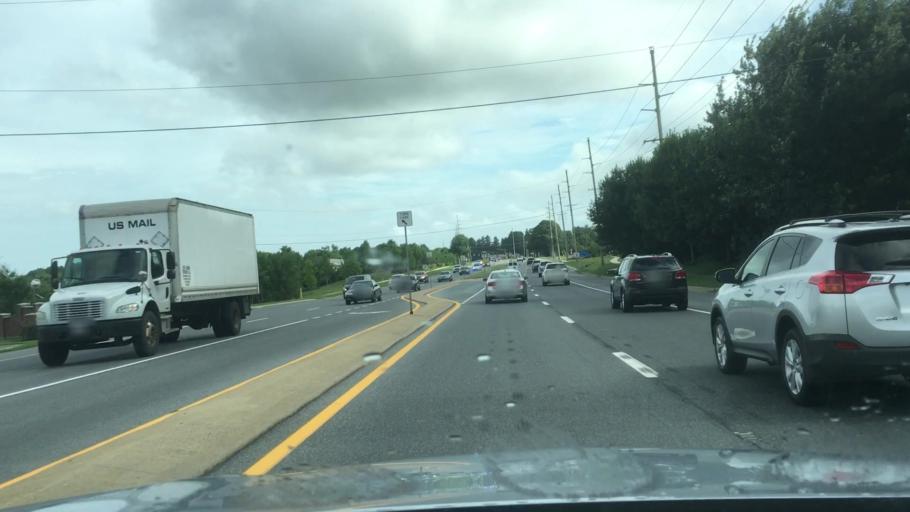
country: US
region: Delaware
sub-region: New Castle County
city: North Star
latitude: 39.7567
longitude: -75.7034
